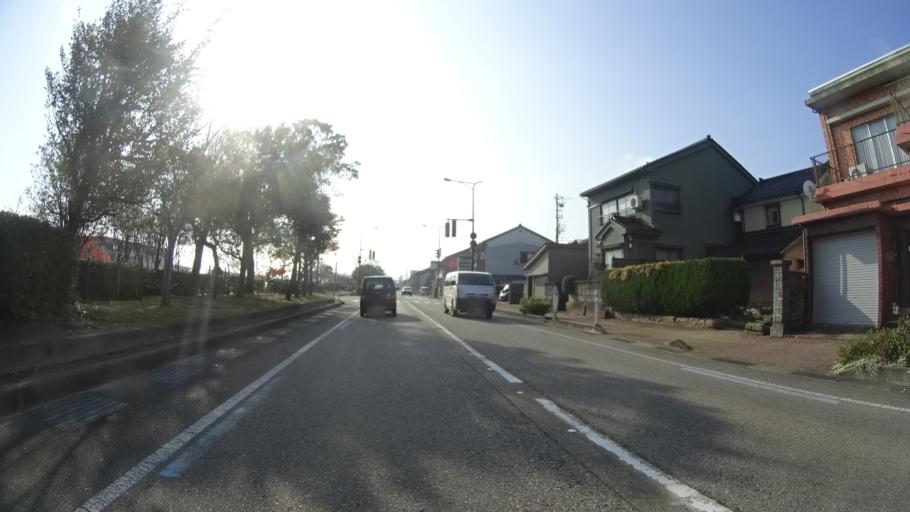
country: JP
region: Toyama
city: Himi
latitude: 36.8579
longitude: 136.9891
